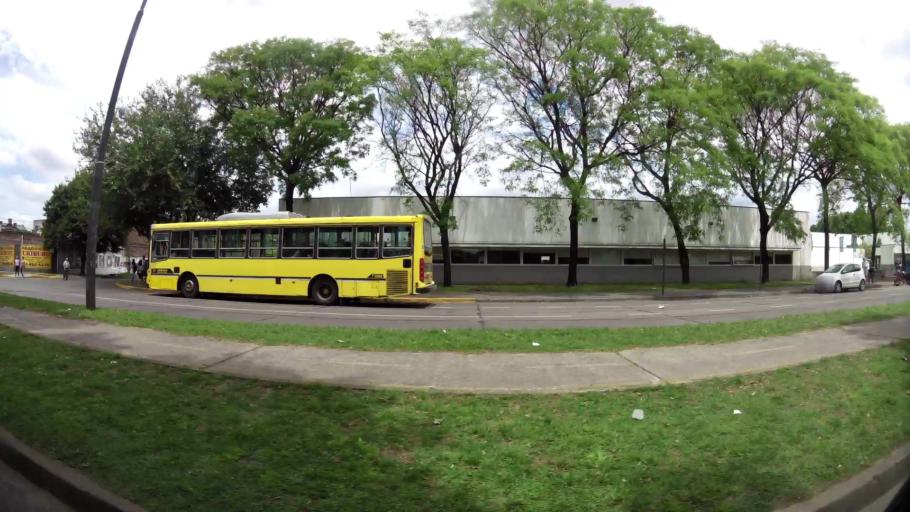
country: AR
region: Santa Fe
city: Gobernador Galvez
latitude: -32.9905
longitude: -60.6424
